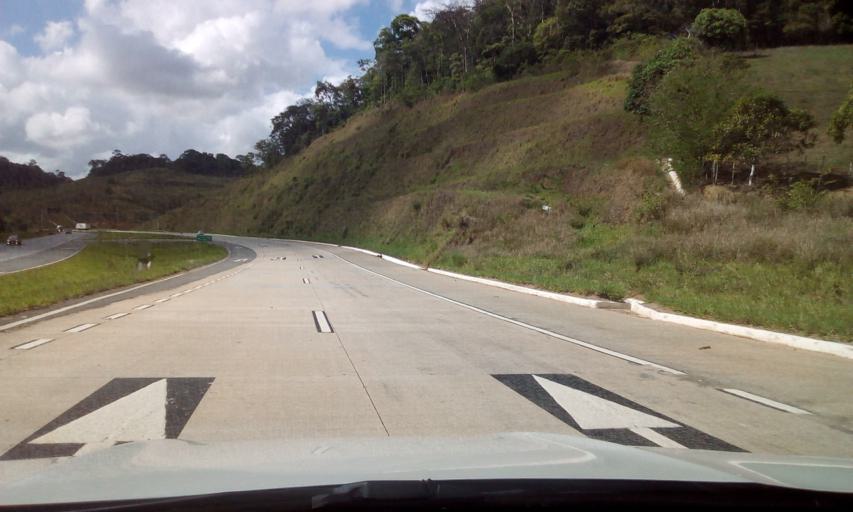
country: BR
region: Pernambuco
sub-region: Palmares
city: Palmares
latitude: -8.7325
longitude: -35.6094
